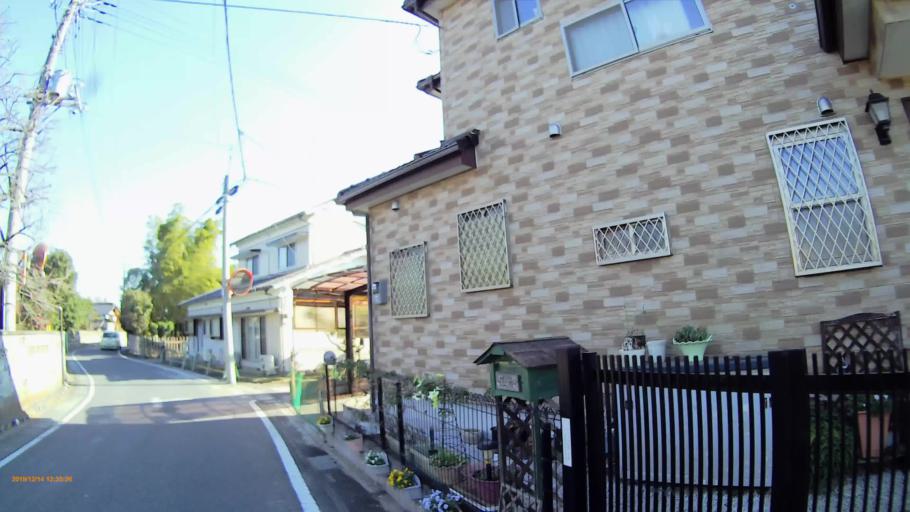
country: JP
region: Saitama
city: Fukiage-fujimi
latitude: 36.1044
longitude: 139.4386
